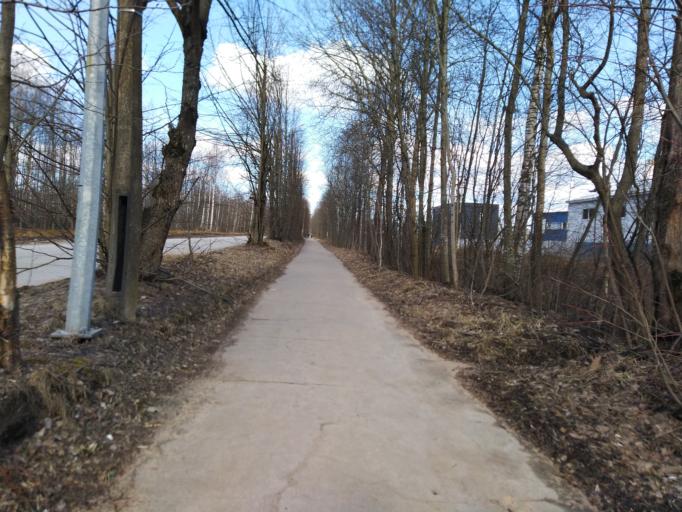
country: RU
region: Leningrad
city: Novoye Devyatkino
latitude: 60.0966
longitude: 30.4756
